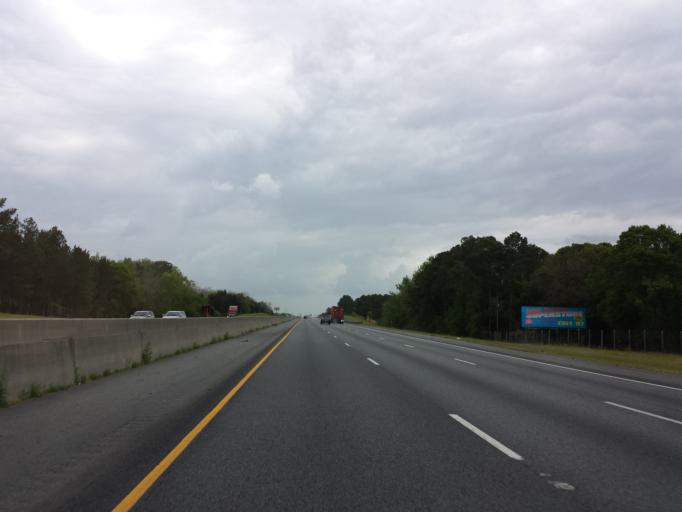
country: US
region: Georgia
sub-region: Tift County
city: Tifton
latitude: 31.5171
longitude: -83.5166
